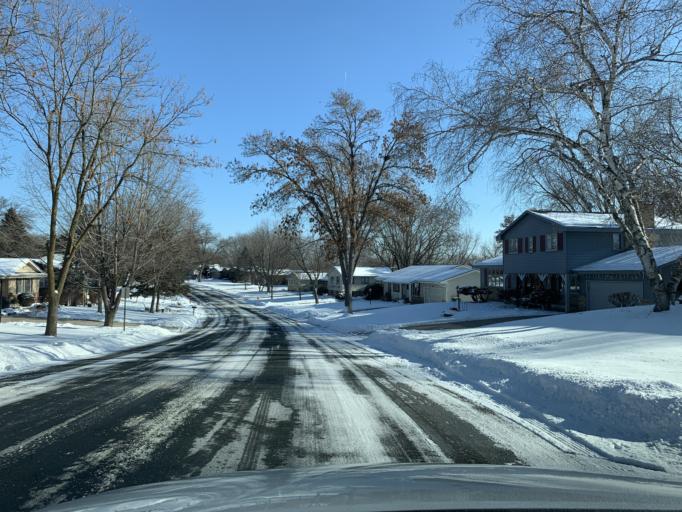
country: US
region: Minnesota
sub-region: Scott County
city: Savage
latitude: 44.8212
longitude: -93.3433
